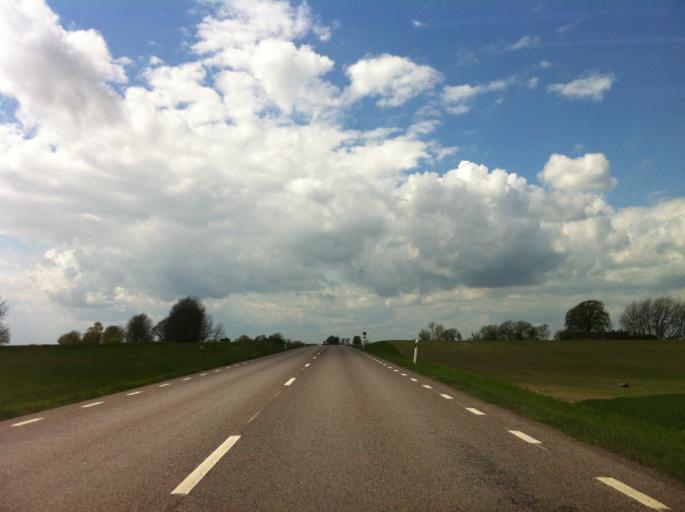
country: SE
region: Skane
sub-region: Eslovs Kommun
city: Stehag
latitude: 55.8545
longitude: 13.3809
